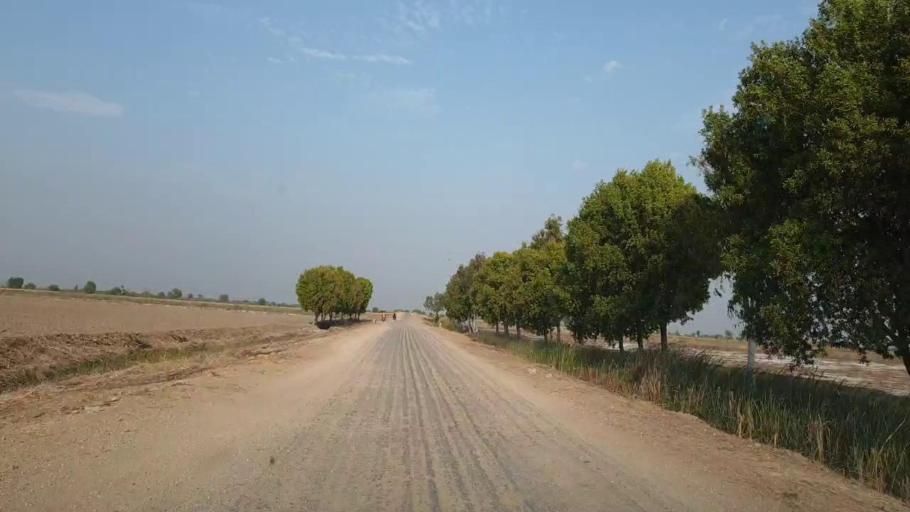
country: PK
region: Sindh
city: Pithoro
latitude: 25.5846
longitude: 69.2694
